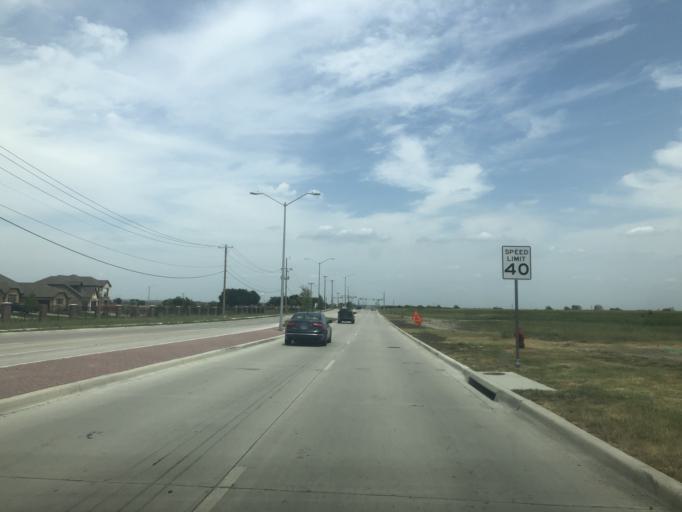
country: US
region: Texas
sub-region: Tarrant County
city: Saginaw
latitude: 32.8837
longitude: -97.3697
